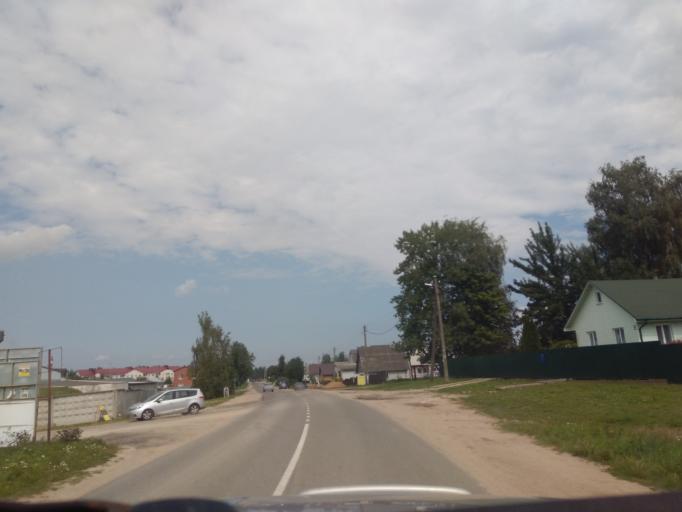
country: BY
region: Minsk
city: Khatsyezhyna
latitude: 53.9075
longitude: 27.3041
